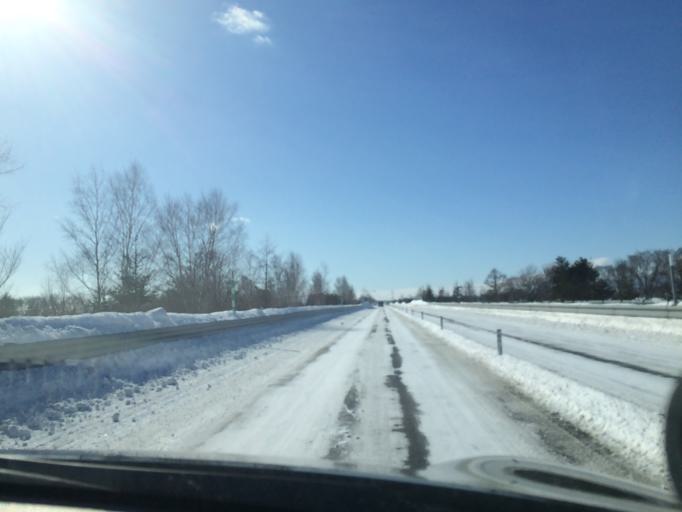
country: JP
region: Hokkaido
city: Chitose
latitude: 42.8755
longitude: 141.6163
